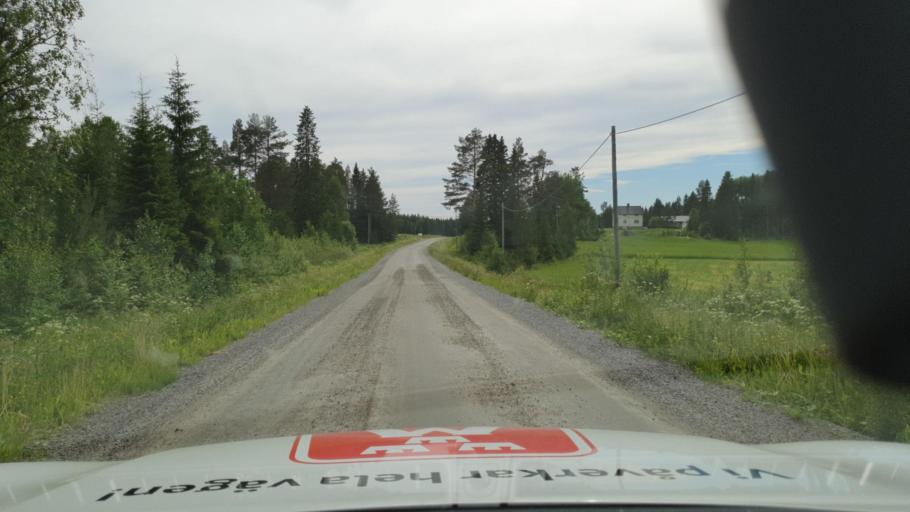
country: SE
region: Vaesterbotten
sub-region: Skelleftea Kommun
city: Burea
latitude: 64.4627
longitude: 21.0404
